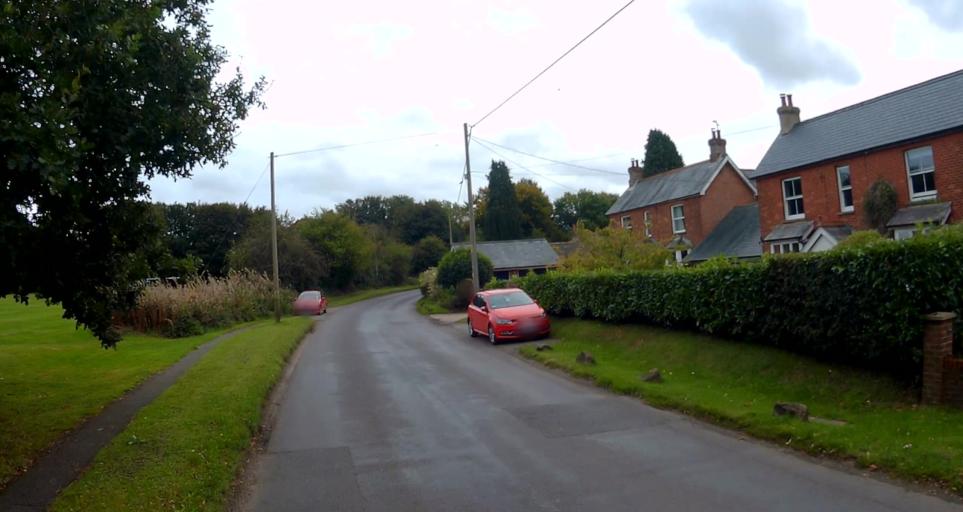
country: GB
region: England
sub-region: Hampshire
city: Four Marks
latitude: 51.1279
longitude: -1.0622
